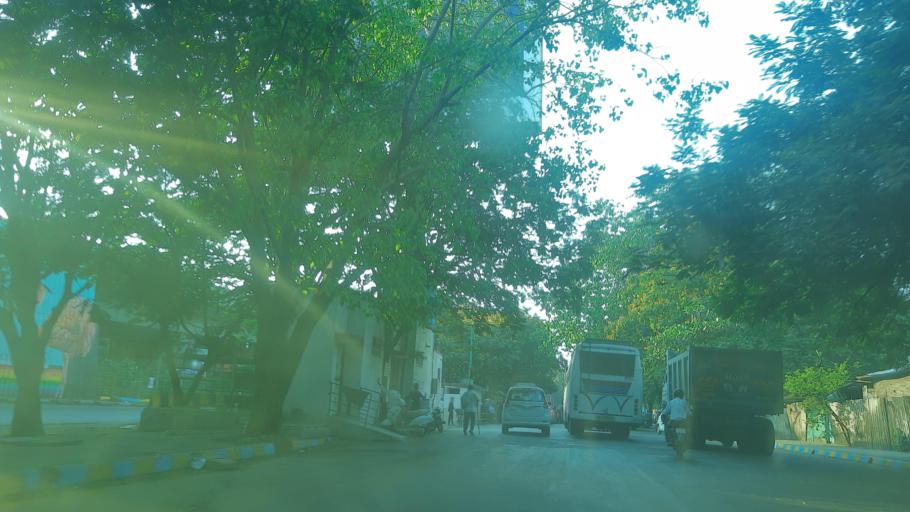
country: IN
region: Maharashtra
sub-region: Thane
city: Thane
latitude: 19.1872
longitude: 72.9644
